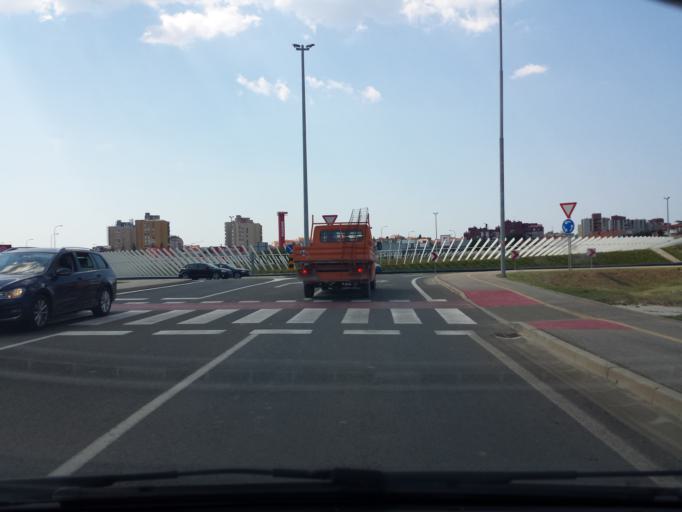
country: HR
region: Istarska
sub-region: Grad Pula
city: Pula
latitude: 44.8817
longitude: 13.8646
